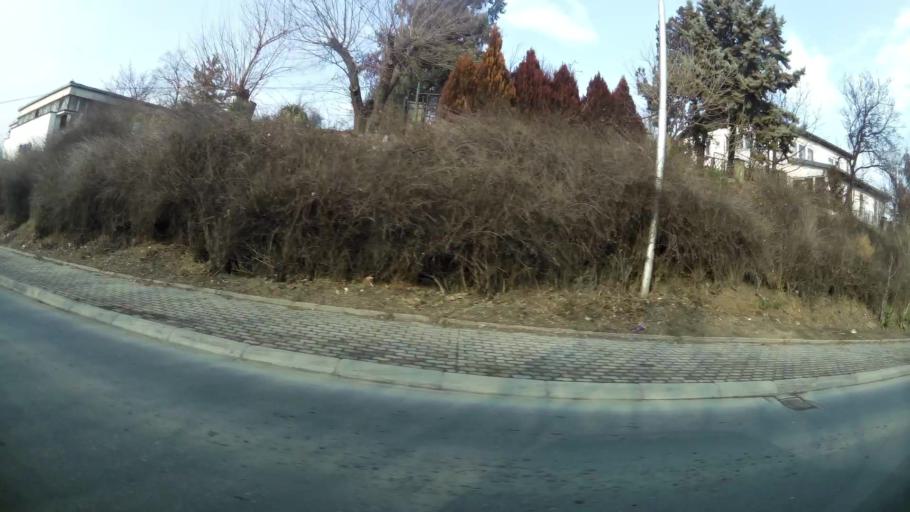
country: MK
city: Creshevo
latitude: 42.0037
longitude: 21.4961
